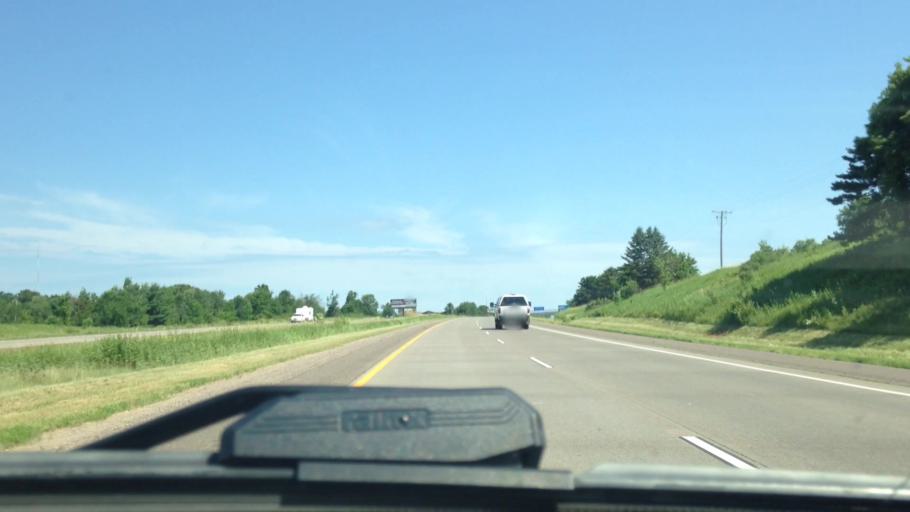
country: US
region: Wisconsin
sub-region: Barron County
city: Rice Lake
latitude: 45.4953
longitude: -91.7639
